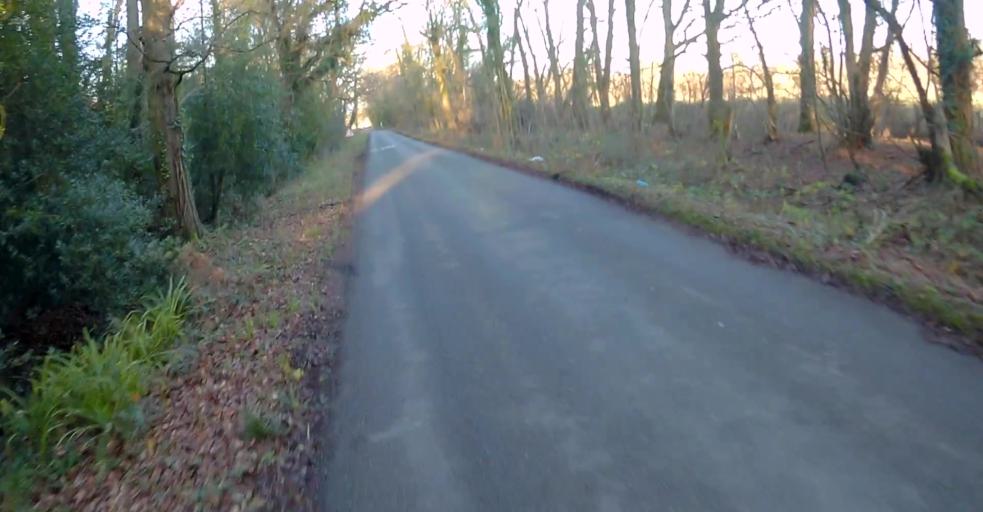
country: GB
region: England
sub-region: Hampshire
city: Hook
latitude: 51.2928
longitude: -0.9776
